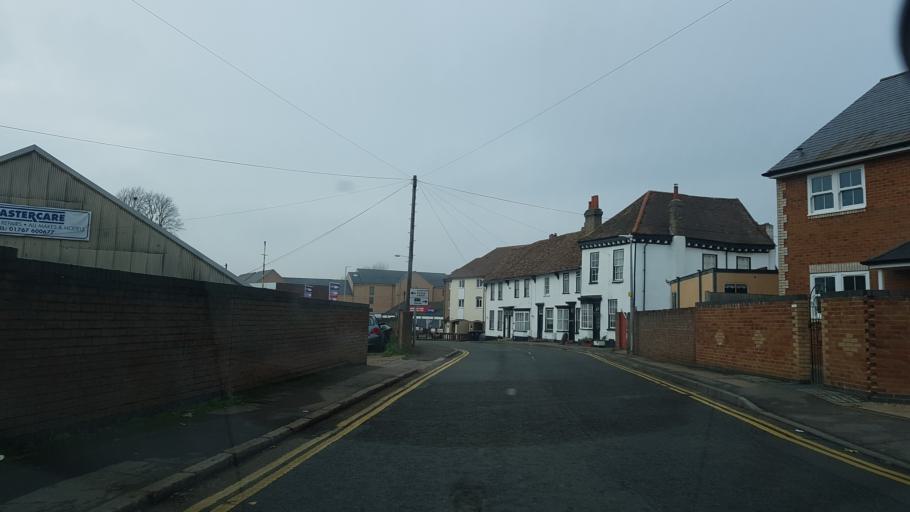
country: GB
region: England
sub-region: Central Bedfordshire
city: Biggleswade
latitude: 52.0915
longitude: -0.2666
